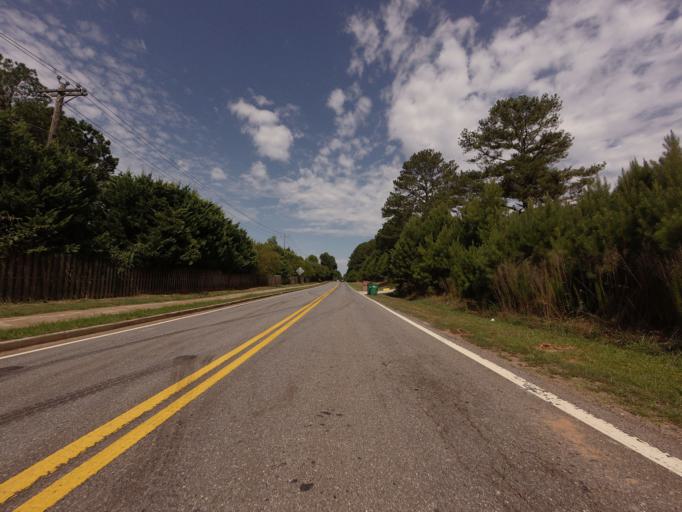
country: US
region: Georgia
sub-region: Fulton County
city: Johns Creek
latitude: 34.0424
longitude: -84.1603
